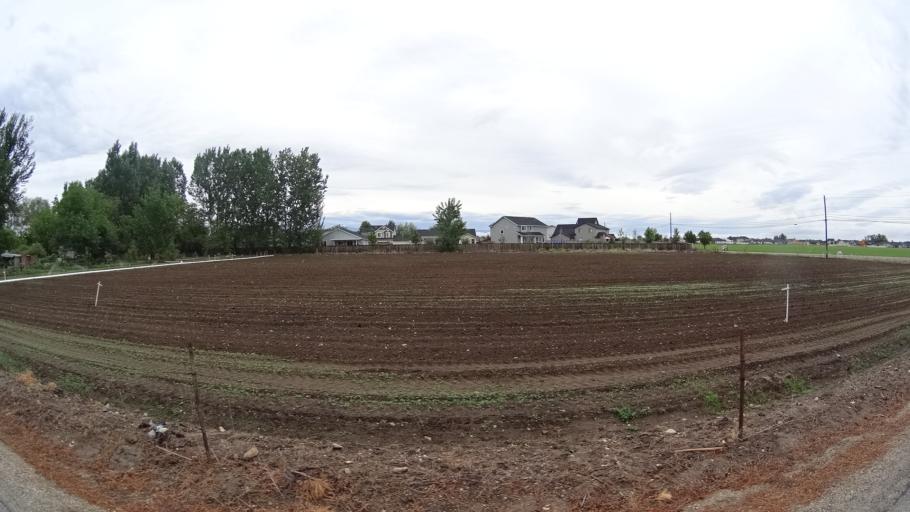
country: US
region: Idaho
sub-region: Ada County
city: Star
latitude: 43.7072
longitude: -116.4884
